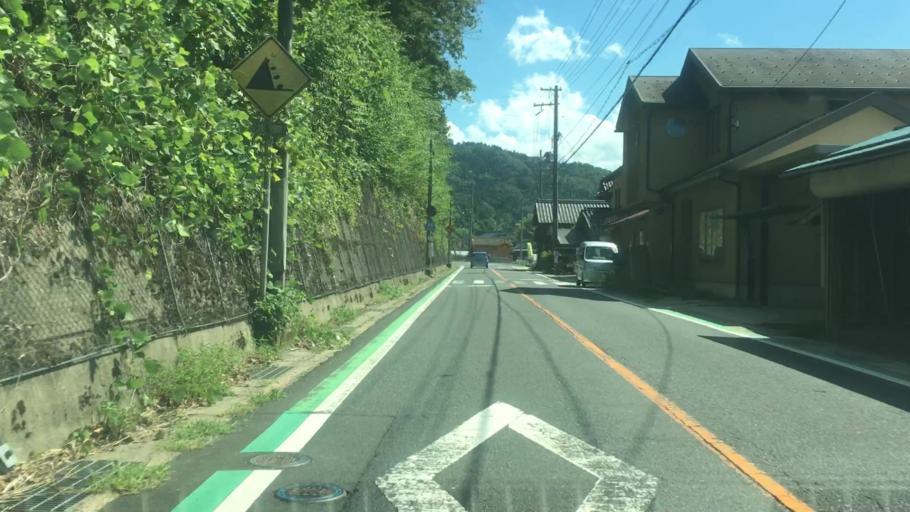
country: JP
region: Hyogo
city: Toyooka
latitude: 35.5956
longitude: 134.9055
